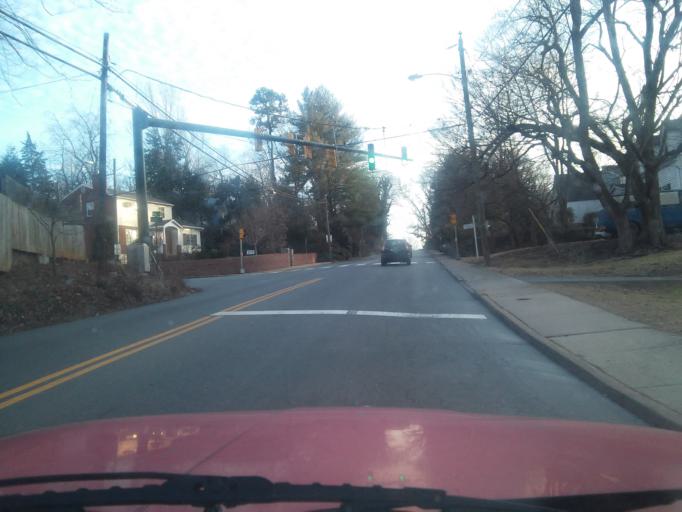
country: US
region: Virginia
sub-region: City of Charlottesville
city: Charlottesville
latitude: 38.0443
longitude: -78.4703
